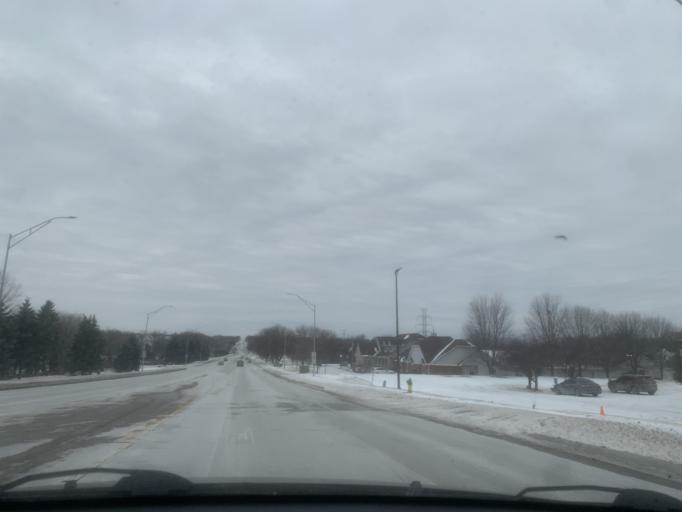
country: US
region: Nebraska
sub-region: Douglas County
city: Ralston
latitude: 41.2778
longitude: -96.0870
